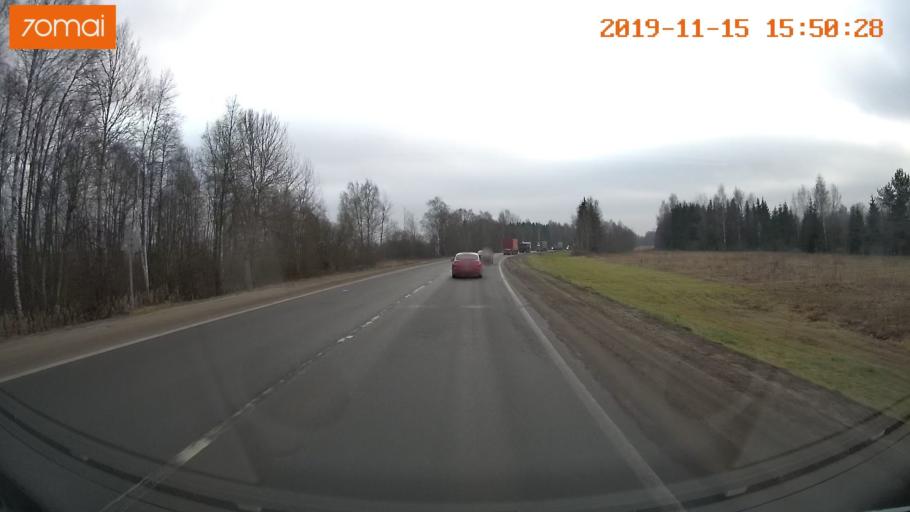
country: RU
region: Jaroslavl
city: Yaroslavl
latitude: 57.9051
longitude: 40.0134
